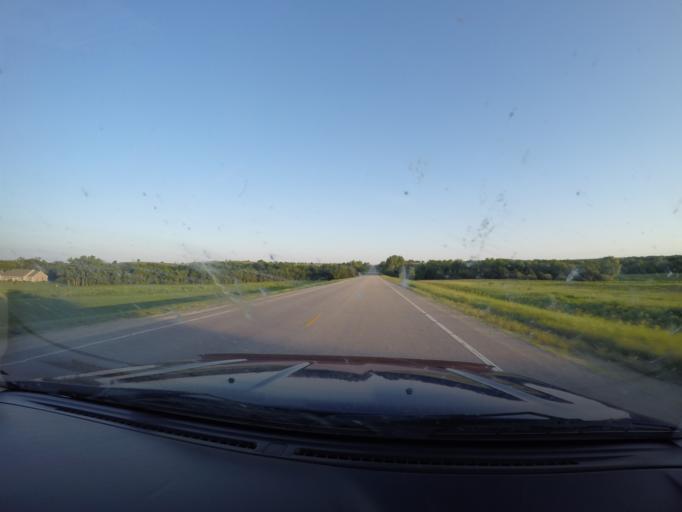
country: US
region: Kansas
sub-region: Riley County
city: Manhattan
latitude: 39.3848
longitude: -96.7565
